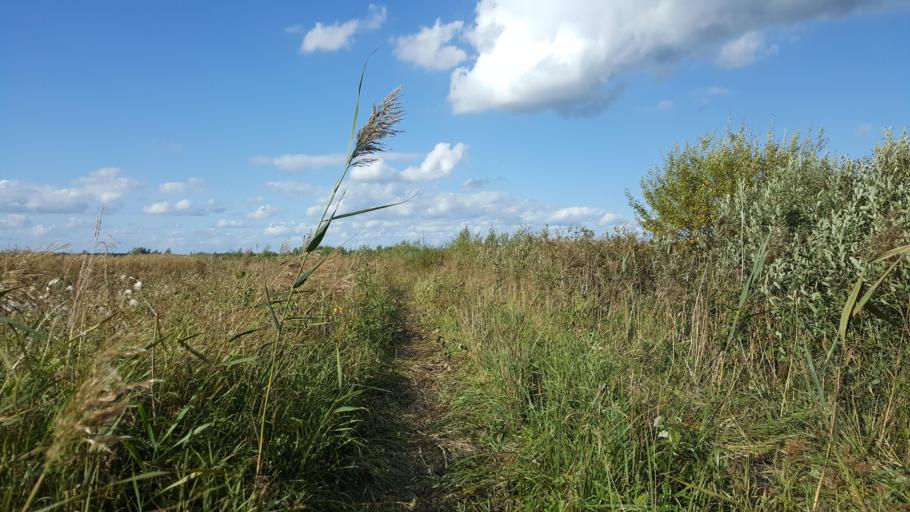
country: BY
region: Brest
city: Kamyanyets
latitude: 52.4551
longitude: 23.9351
